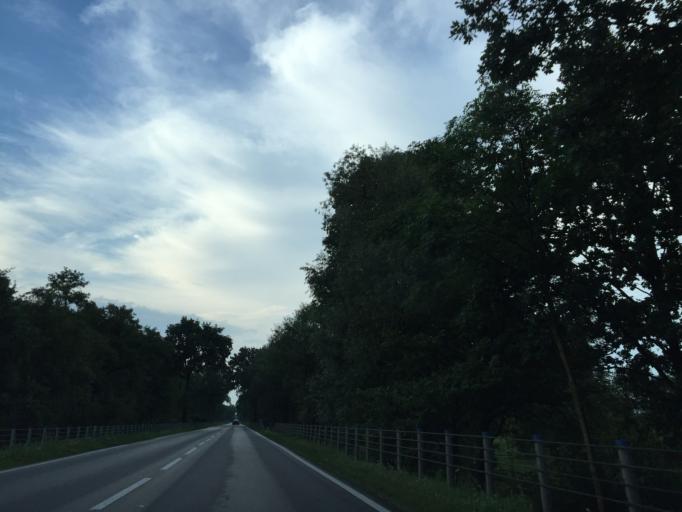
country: PL
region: Masovian Voivodeship
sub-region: Powiat wegrowski
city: Sadowne
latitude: 52.6661
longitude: 21.8489
